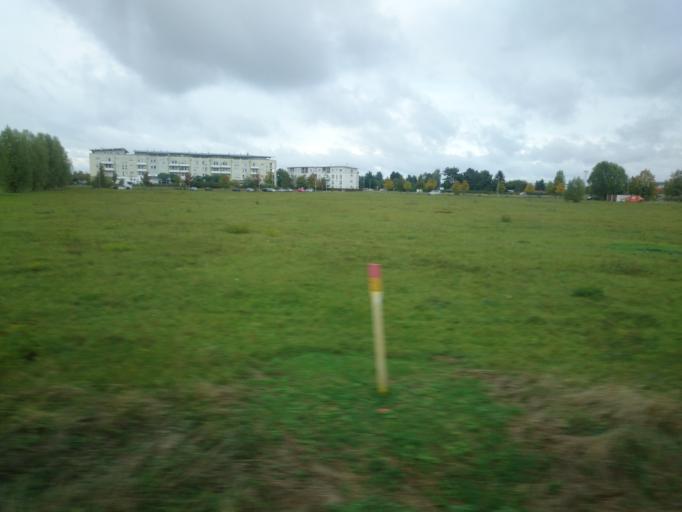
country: DE
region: Saxony-Anhalt
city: Grosskugel
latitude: 51.4120
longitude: 12.1546
